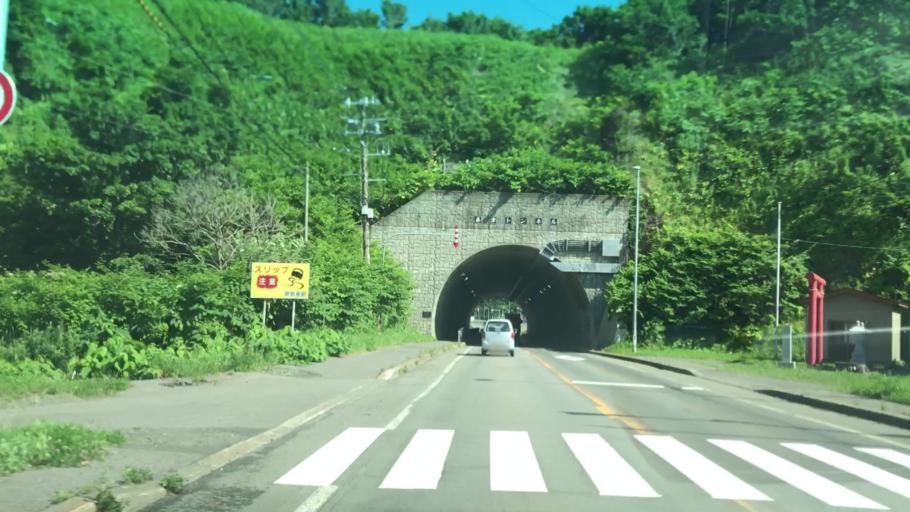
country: JP
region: Hokkaido
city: Iwanai
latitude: 43.0444
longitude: 140.5066
